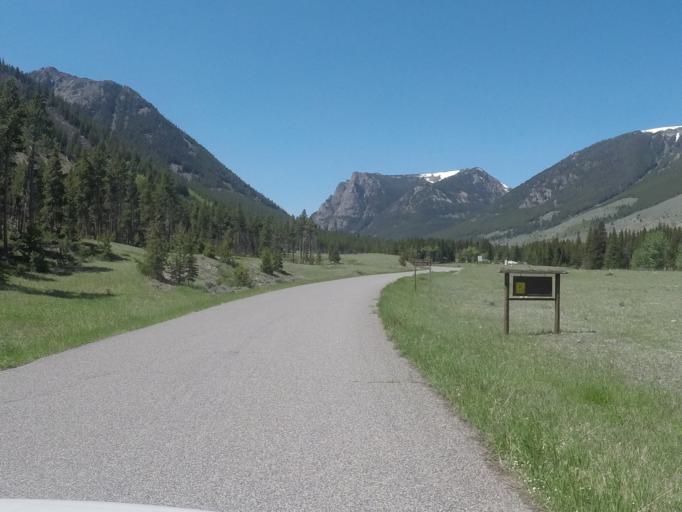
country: US
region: Montana
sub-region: Carbon County
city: Red Lodge
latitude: 45.0621
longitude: -109.3996
